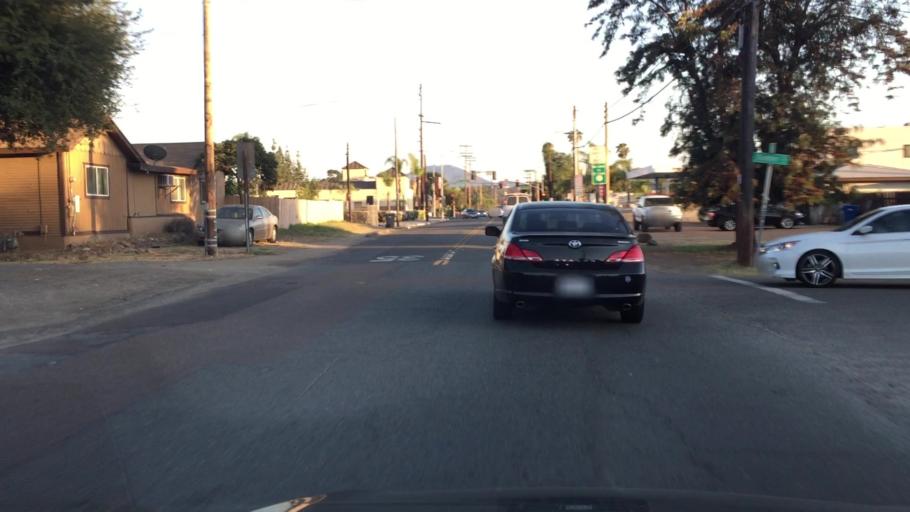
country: US
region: California
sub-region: San Diego County
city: Bostonia
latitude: 32.8091
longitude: -116.9446
